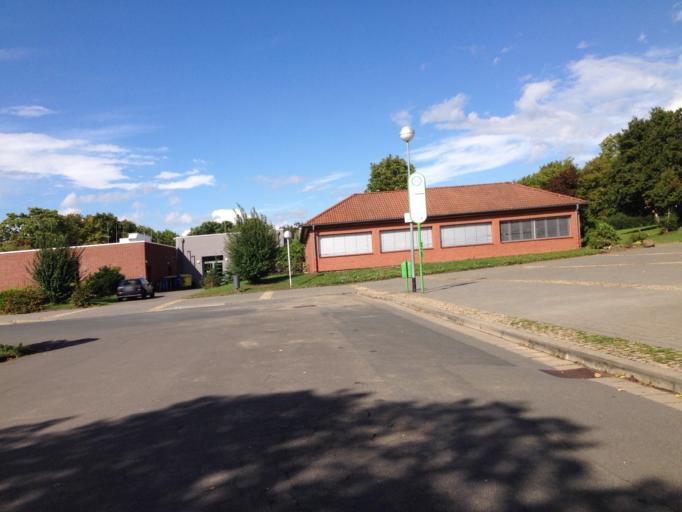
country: DE
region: Hesse
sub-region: Regierungsbezirk Giessen
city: Hungen
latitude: 50.4822
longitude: 8.8988
